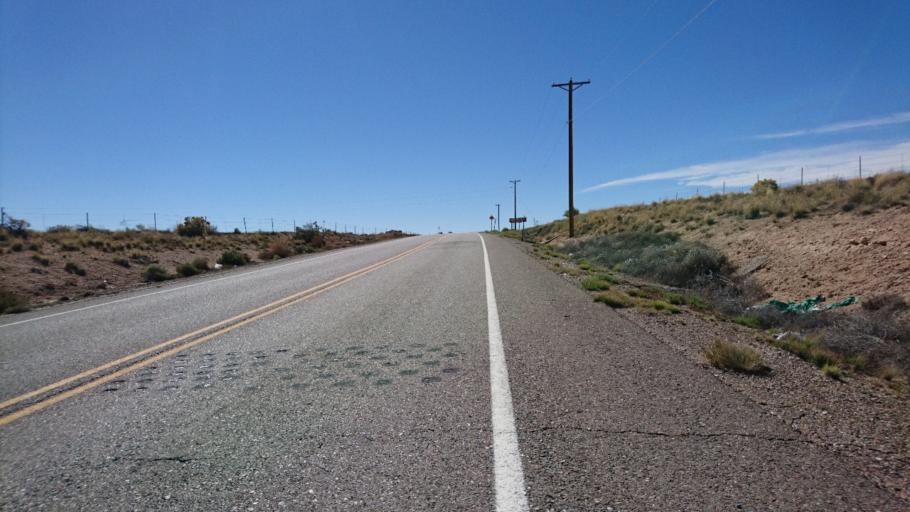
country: US
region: New Mexico
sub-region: Bernalillo County
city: South Valley
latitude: 35.0636
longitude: -106.7951
